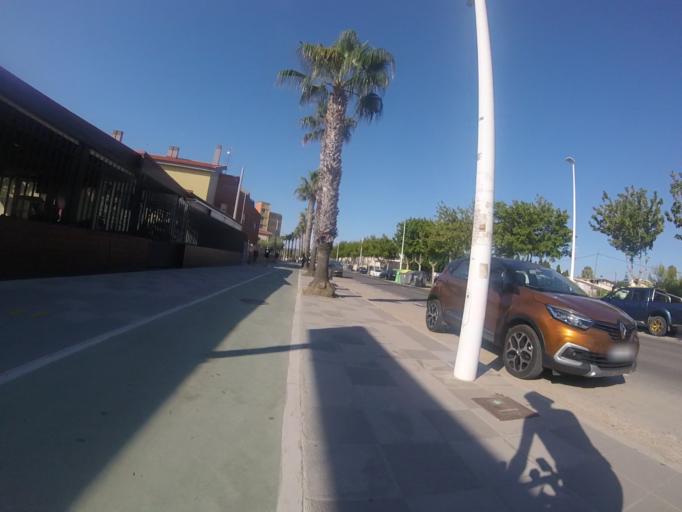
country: ES
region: Valencia
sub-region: Provincia de Castello
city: Benicarlo
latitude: 40.4051
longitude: 0.4205
